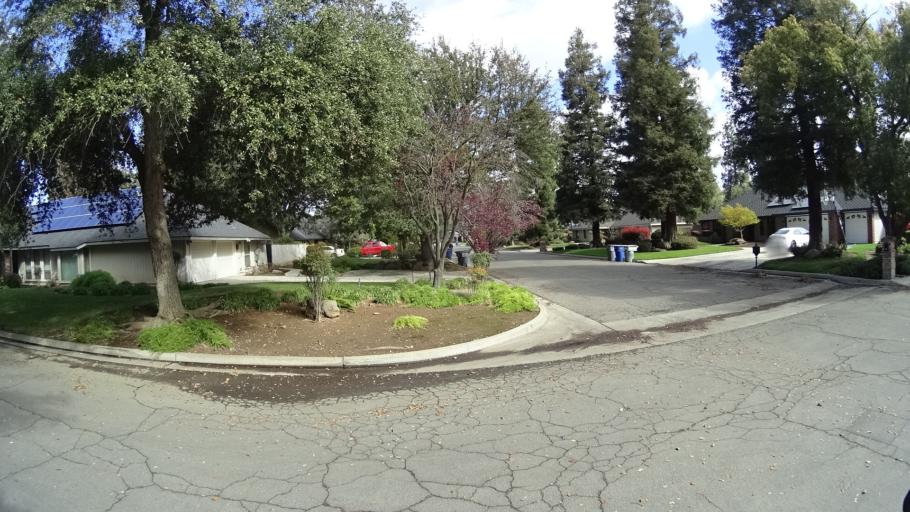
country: US
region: California
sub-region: Fresno County
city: Fresno
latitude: 36.8322
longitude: -119.8453
